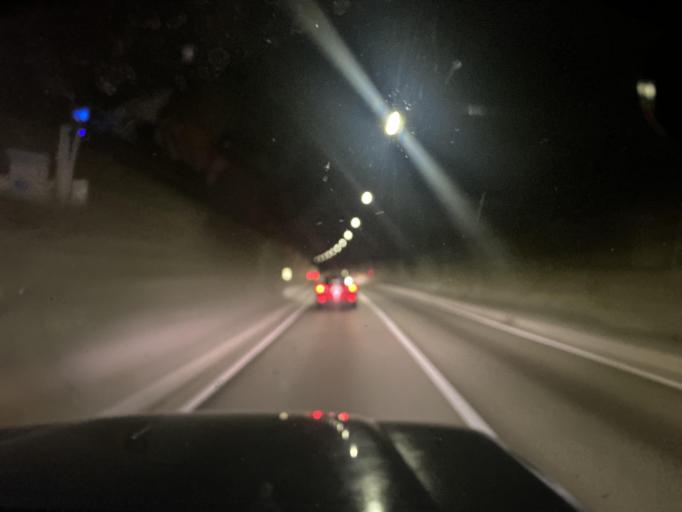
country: JP
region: Nagano
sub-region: Kitaazumi Gun
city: Hakuba
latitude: 36.8033
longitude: 137.9127
